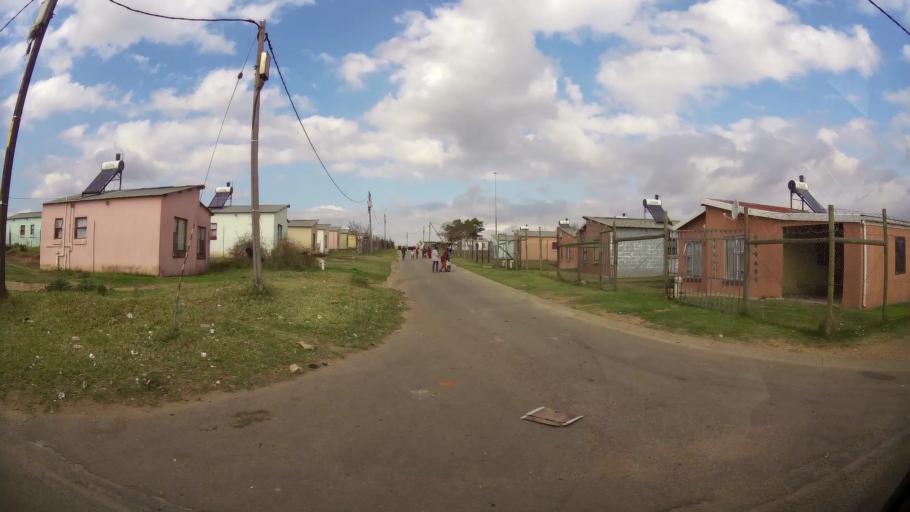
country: ZA
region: Eastern Cape
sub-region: Nelson Mandela Bay Metropolitan Municipality
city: Uitenhage
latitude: -33.7468
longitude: 25.3939
